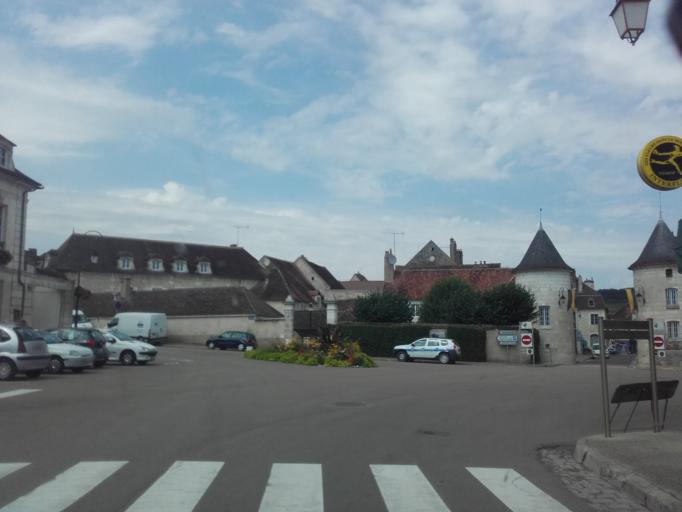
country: FR
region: Bourgogne
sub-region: Departement de l'Yonne
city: Chablis
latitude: 47.8134
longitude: 3.8006
